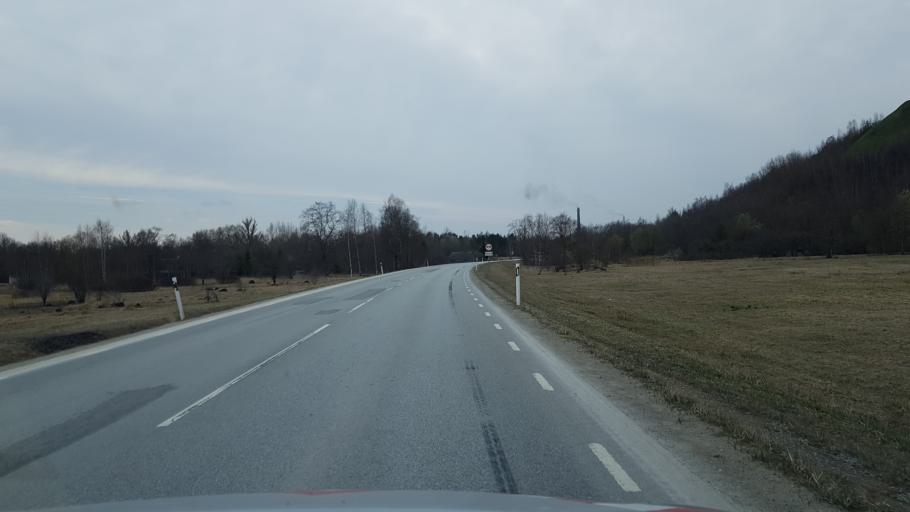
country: EE
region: Ida-Virumaa
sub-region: Kivioli linn
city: Kivioli
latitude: 59.3621
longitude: 26.9607
